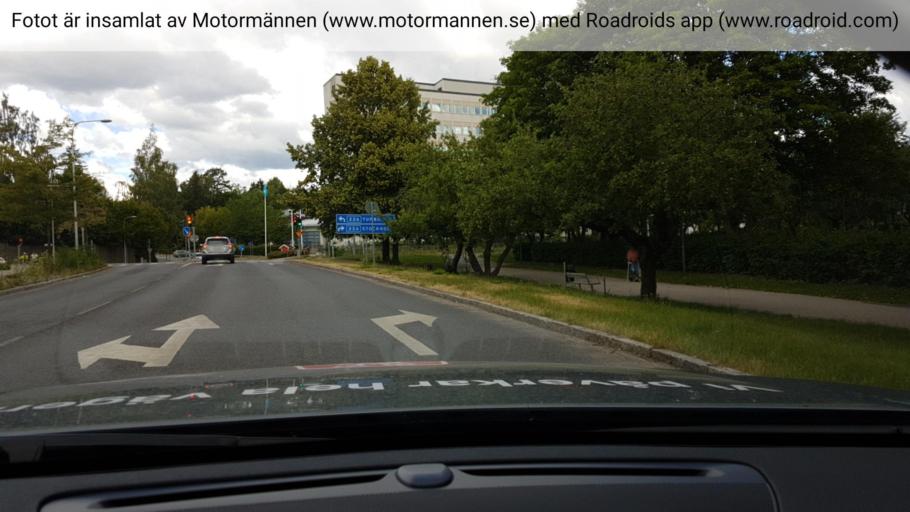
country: SE
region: Stockholm
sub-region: Huddinge Kommun
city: Huddinge
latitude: 59.2429
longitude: 17.9947
